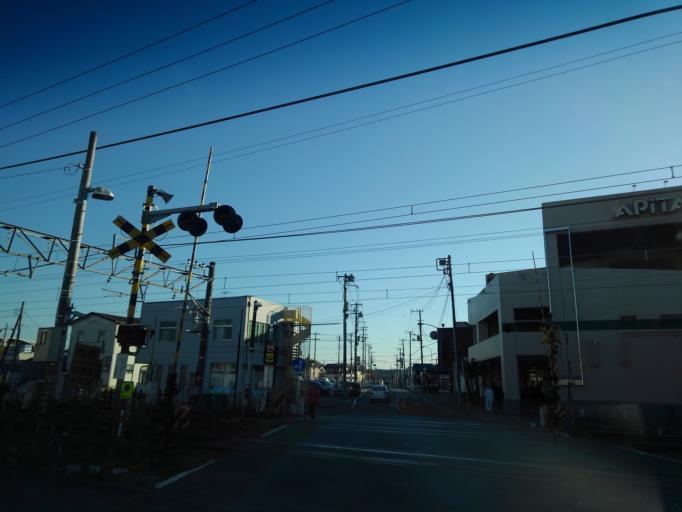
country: JP
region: Chiba
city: Kimitsu
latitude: 35.3327
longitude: 139.8993
